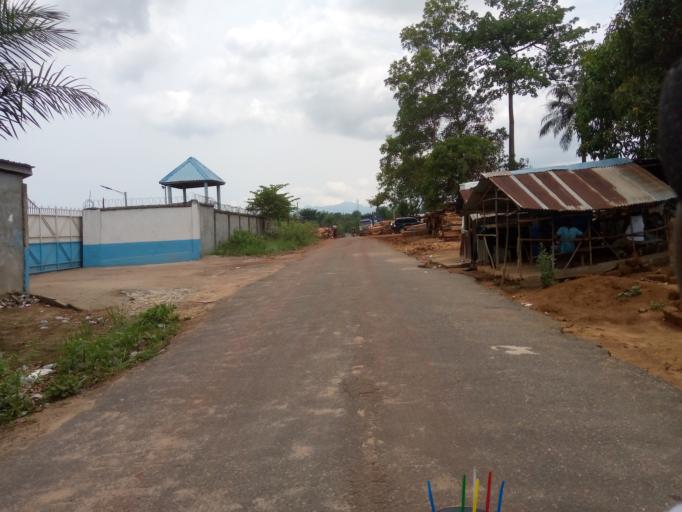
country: SL
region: Western Area
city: Waterloo
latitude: 8.3379
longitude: -12.9927
